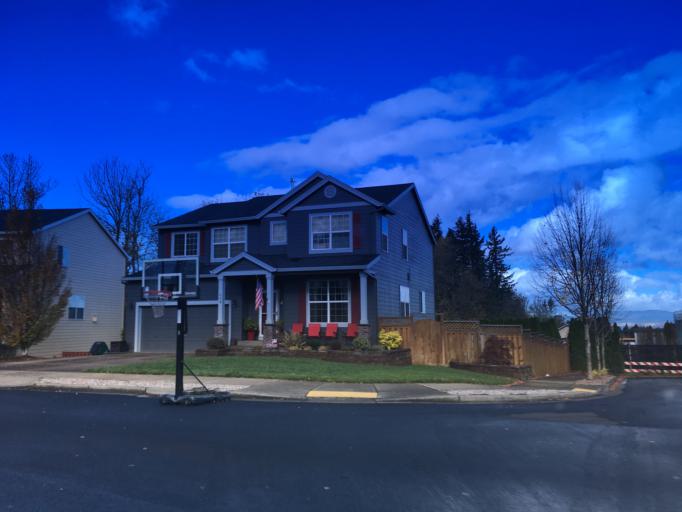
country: US
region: Oregon
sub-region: Multnomah County
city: Troutdale
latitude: 45.5073
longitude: -122.3812
